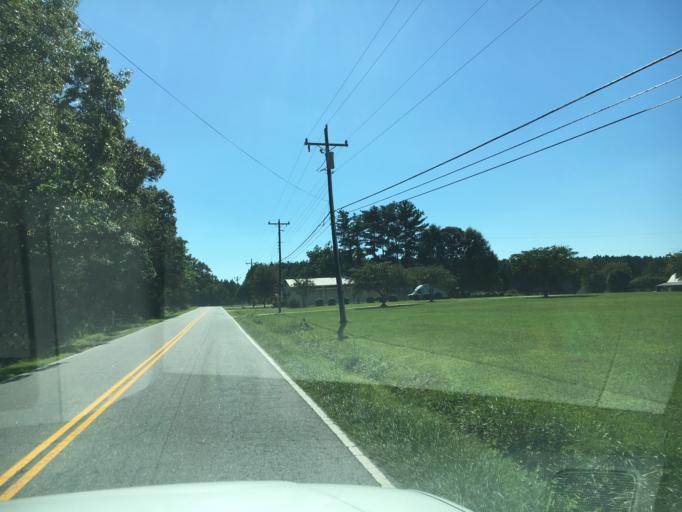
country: US
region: South Carolina
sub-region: Greenville County
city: Five Forks
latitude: 34.8471
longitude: -82.1563
